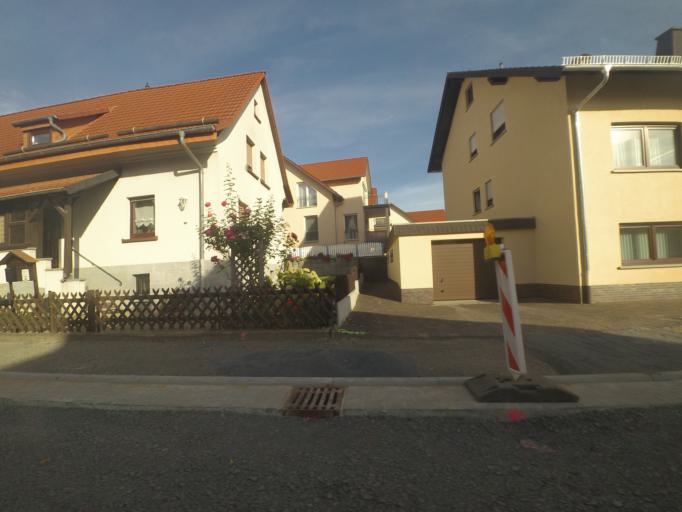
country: DE
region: Hesse
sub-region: Regierungsbezirk Kassel
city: Flieden
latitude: 50.4250
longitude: 9.5678
